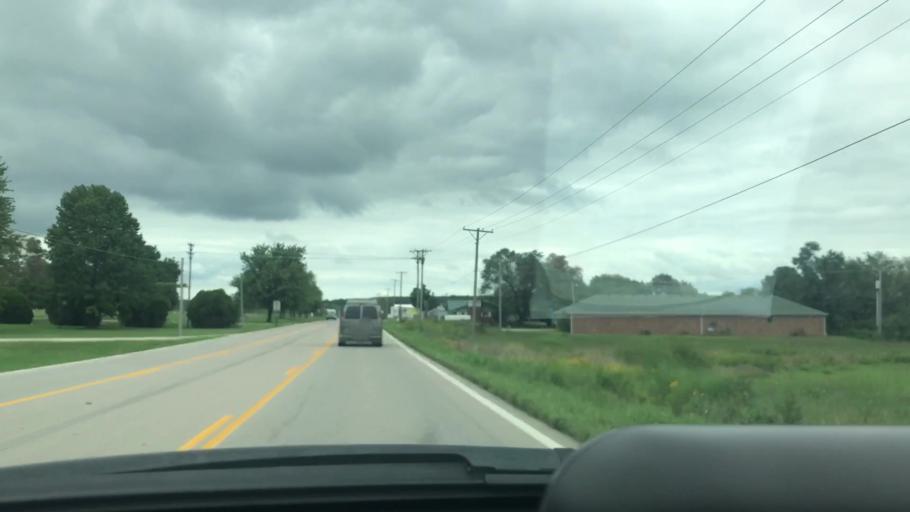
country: US
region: Missouri
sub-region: Dallas County
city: Buffalo
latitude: 37.6539
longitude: -93.1038
